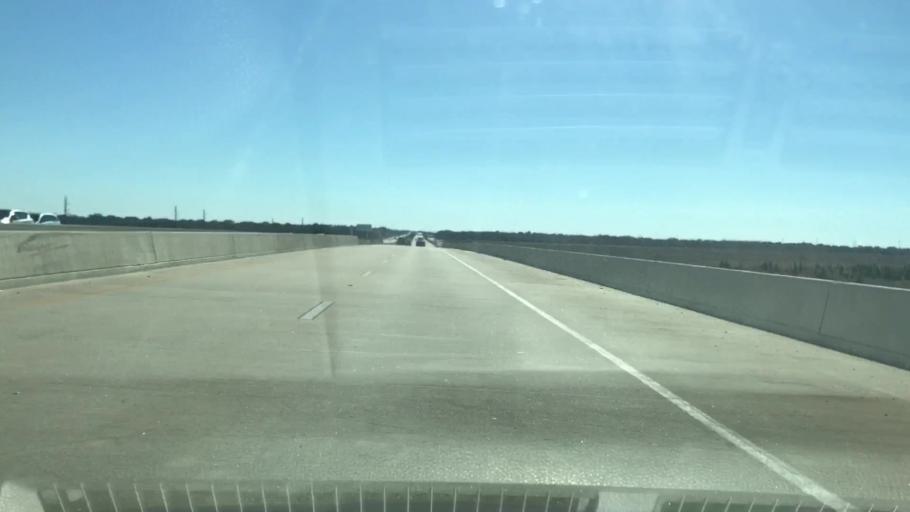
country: US
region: Texas
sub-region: Harris County
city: Cypress
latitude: 29.9782
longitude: -95.7697
